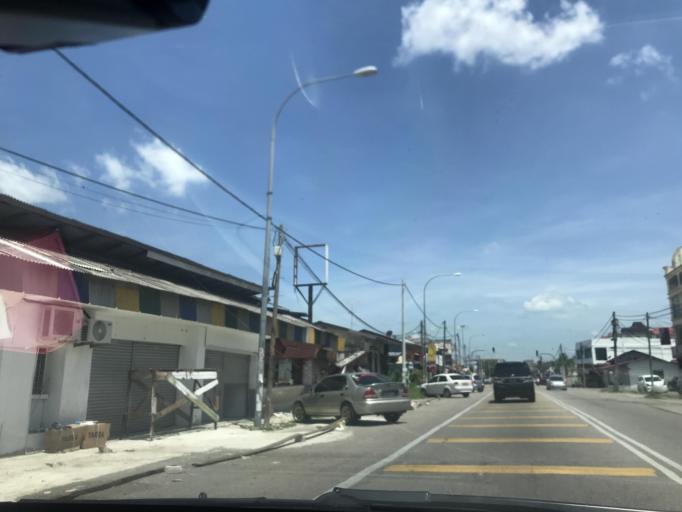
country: MY
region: Kelantan
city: Kota Bharu
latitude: 6.1248
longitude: 102.2559
